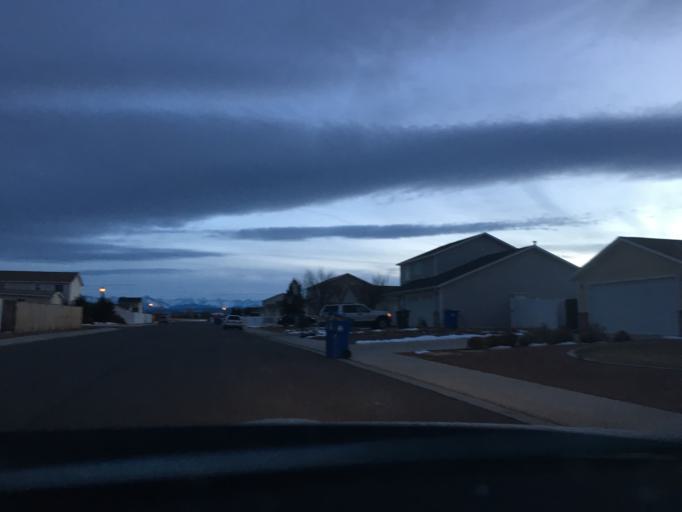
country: US
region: Colorado
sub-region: Montrose County
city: Montrose
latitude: 38.4875
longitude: -107.8423
